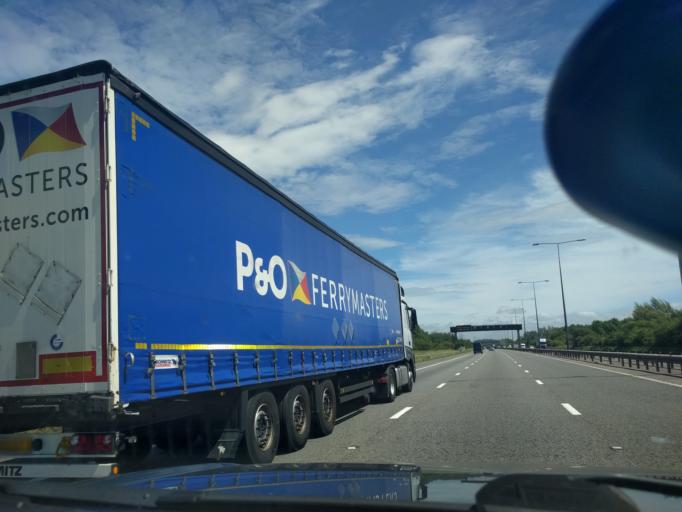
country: GB
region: Wales
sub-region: Monmouthshire
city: Caldicot
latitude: 51.5808
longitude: -2.7598
